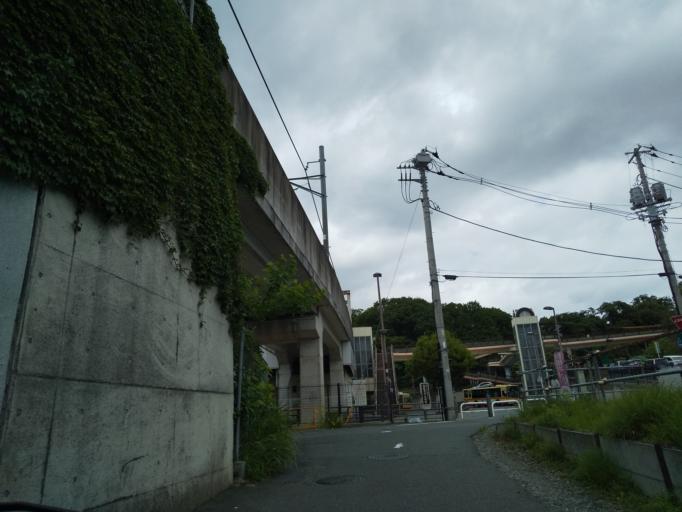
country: JP
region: Kanagawa
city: Zama
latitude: 35.5572
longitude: 139.3636
